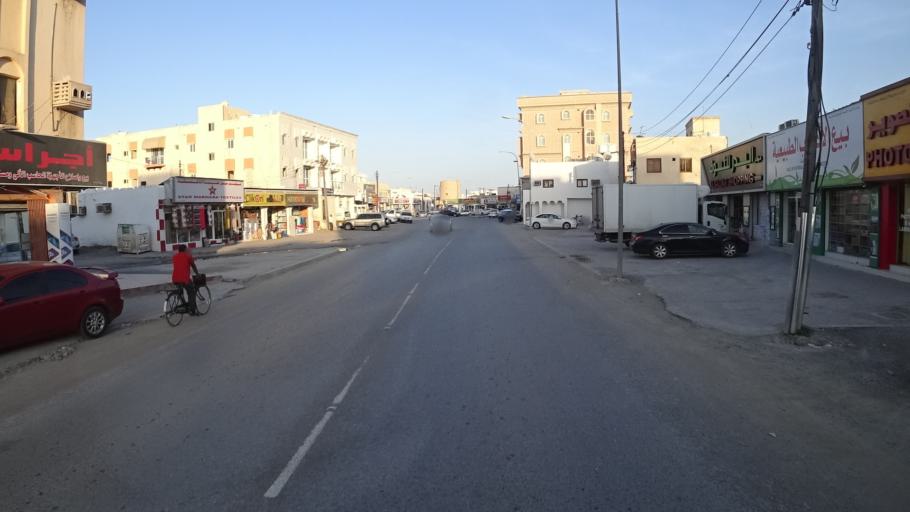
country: OM
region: Al Batinah
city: Barka'
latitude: 23.7072
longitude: 57.8913
